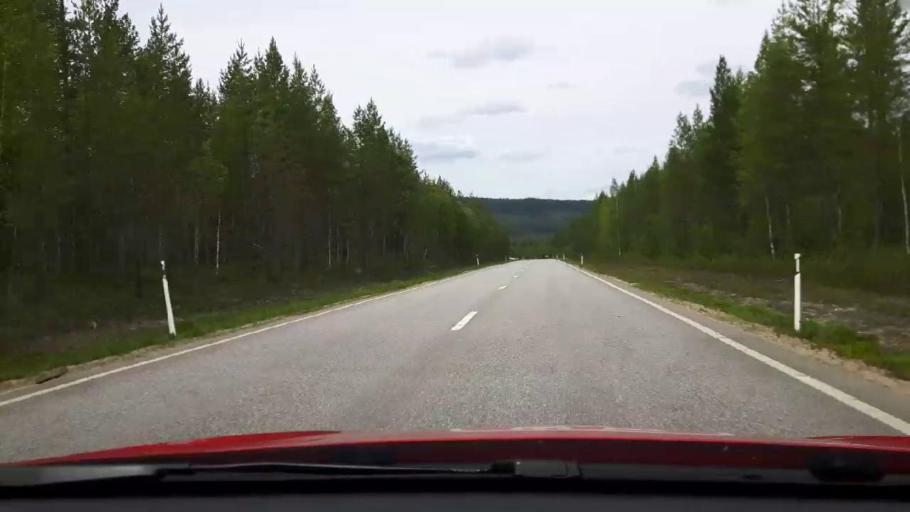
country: SE
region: Jaemtland
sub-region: Harjedalens Kommun
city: Sveg
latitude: 62.0853
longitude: 14.2521
